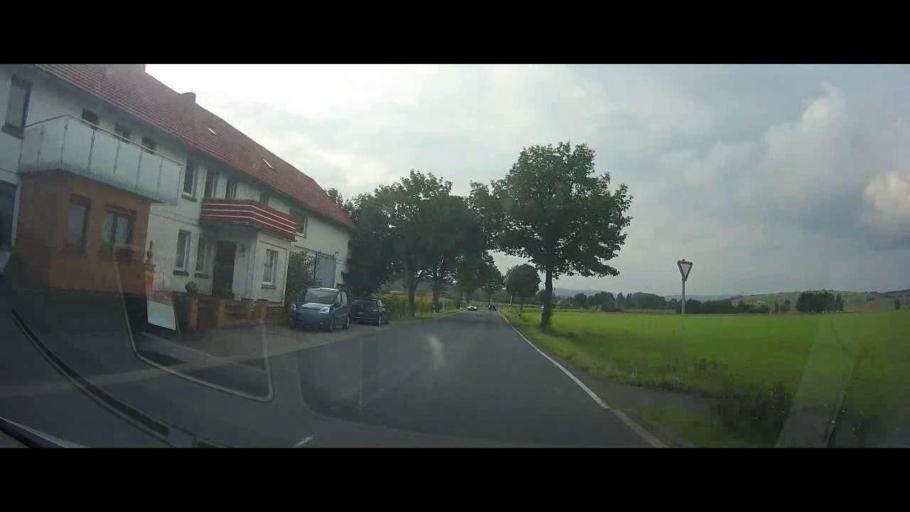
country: DE
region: Lower Saxony
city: Adelebsen
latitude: 51.5888
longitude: 9.6858
